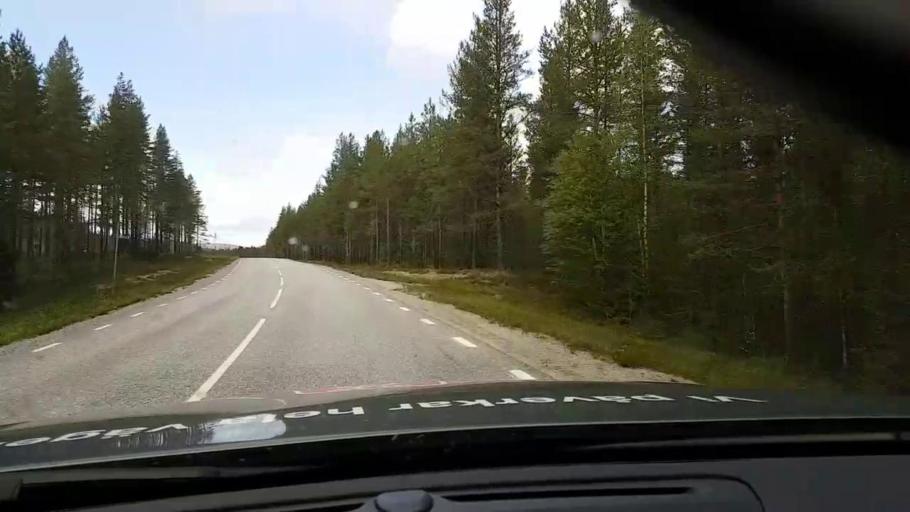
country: SE
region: Vaesternorrland
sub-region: OErnskoeldsviks Kommun
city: Bredbyn
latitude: 63.7031
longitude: 17.7631
